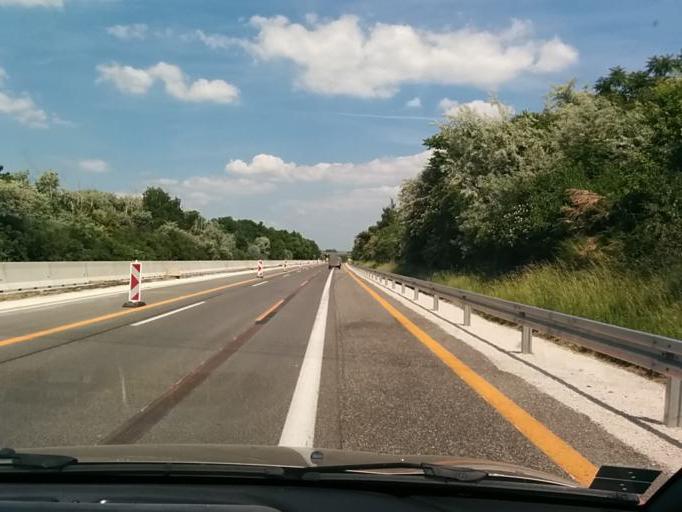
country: SK
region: Trnavsky
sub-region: Okres Trnava
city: Trnava
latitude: 48.3520
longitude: 17.6574
